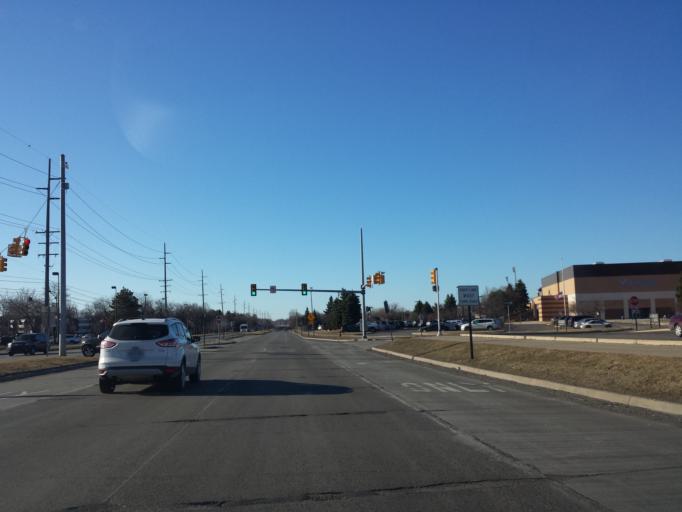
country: US
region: Michigan
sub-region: Oakland County
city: Rochester
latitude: 42.6803
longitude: -83.1535
